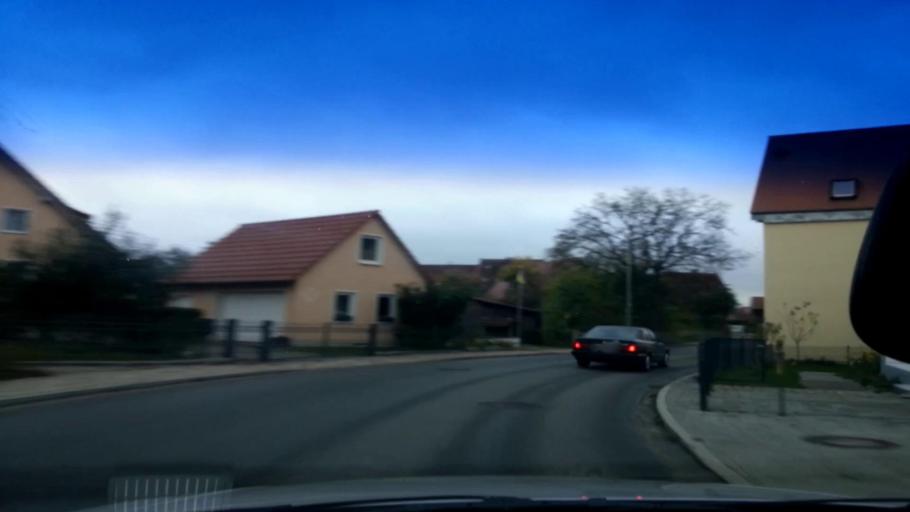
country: DE
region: Bavaria
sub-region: Upper Franconia
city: Litzendorf
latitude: 49.9254
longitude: 11.0073
